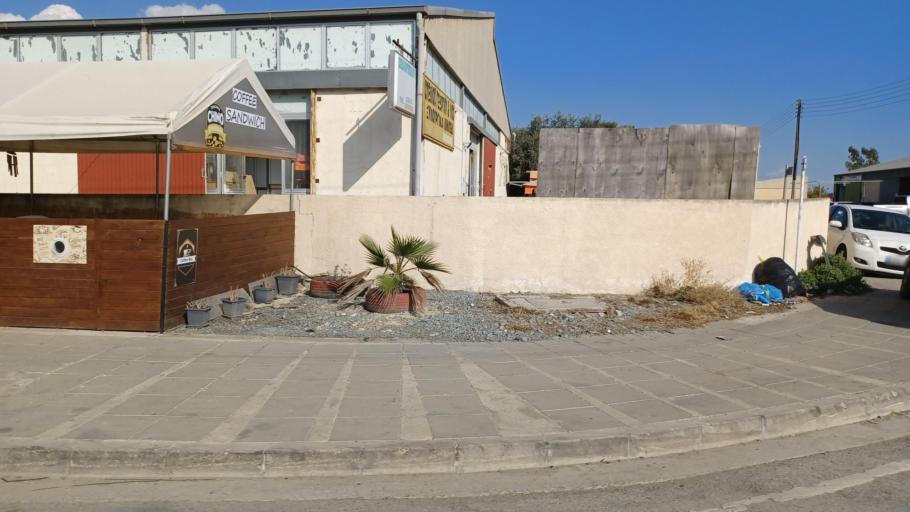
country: CY
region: Larnaka
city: Livadia
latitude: 34.9677
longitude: 33.6274
